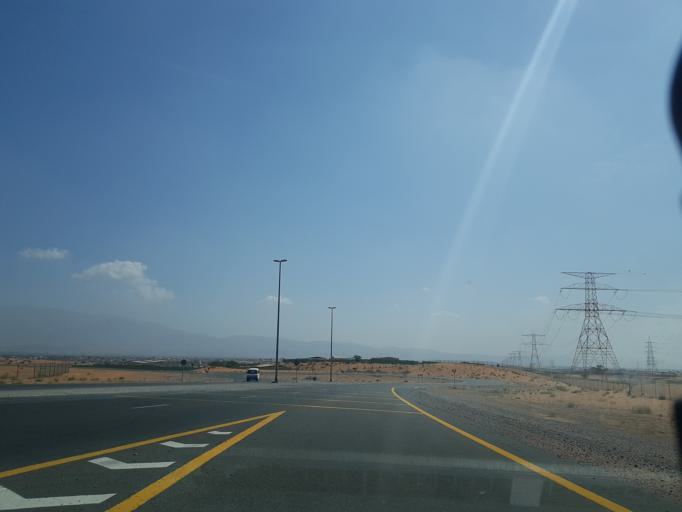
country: AE
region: Ra's al Khaymah
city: Ras al-Khaimah
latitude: 25.6932
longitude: 55.9270
